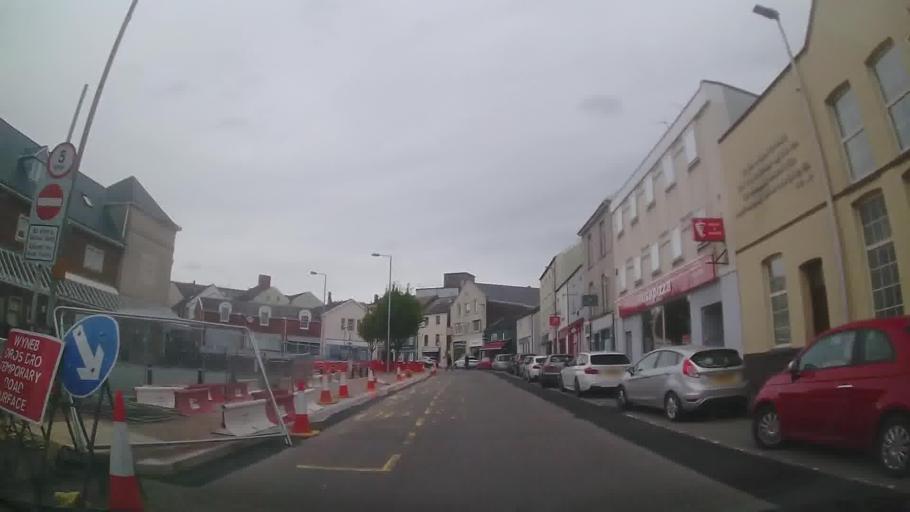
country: GB
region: Wales
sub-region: Carmarthenshire
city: Carmarthen
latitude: 51.8554
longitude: -4.3085
